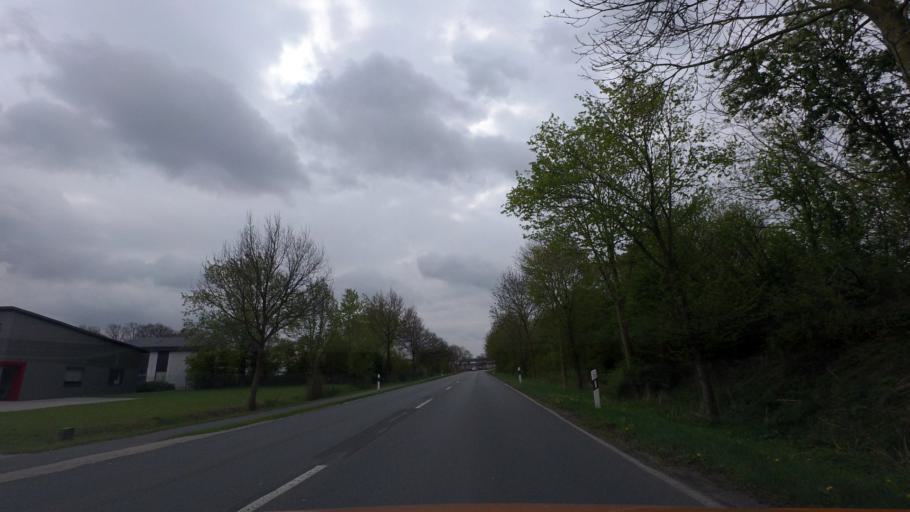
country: DE
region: Lower Saxony
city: Wardenburg
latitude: 53.0486
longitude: 8.2060
